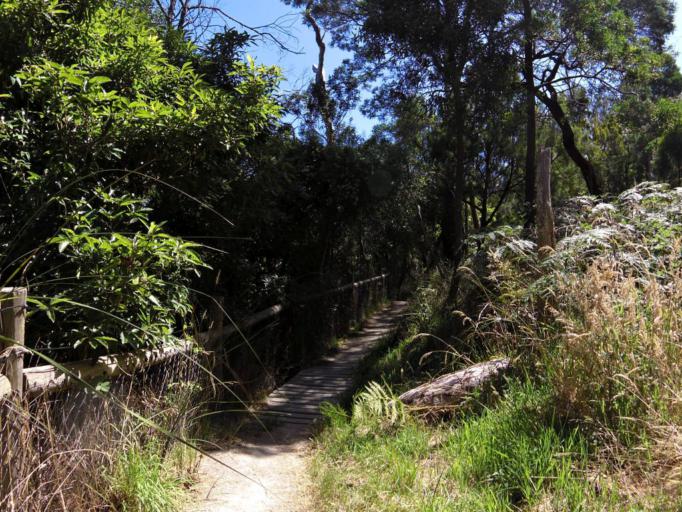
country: AU
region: Victoria
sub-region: Mornington Peninsula
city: Moorooduc
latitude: -38.2032
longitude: 145.1084
